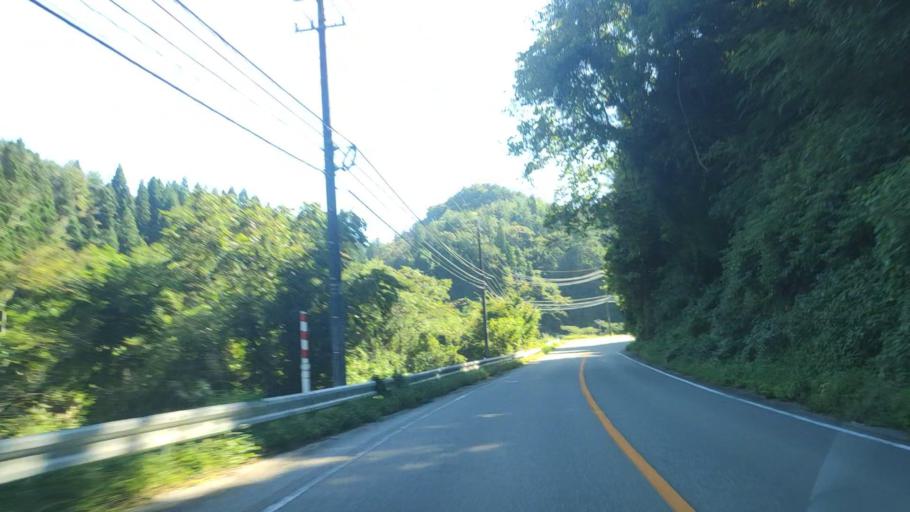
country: JP
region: Ishikawa
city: Nanao
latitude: 37.3305
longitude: 137.2087
